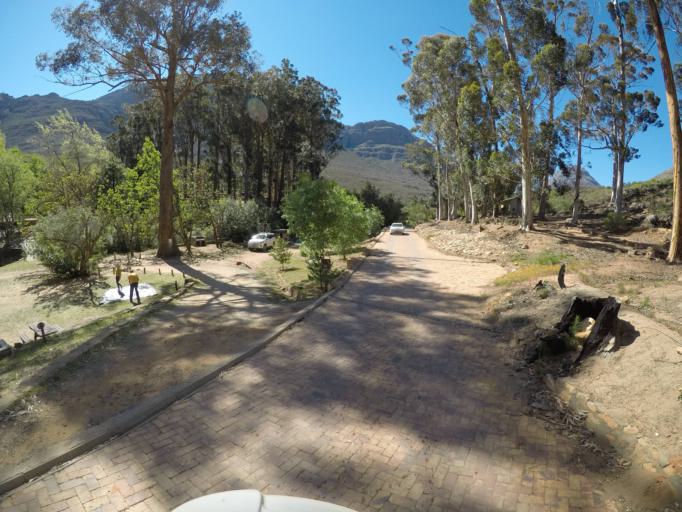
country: ZA
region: Western Cape
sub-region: West Coast District Municipality
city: Clanwilliam
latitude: -32.3744
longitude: 19.0613
